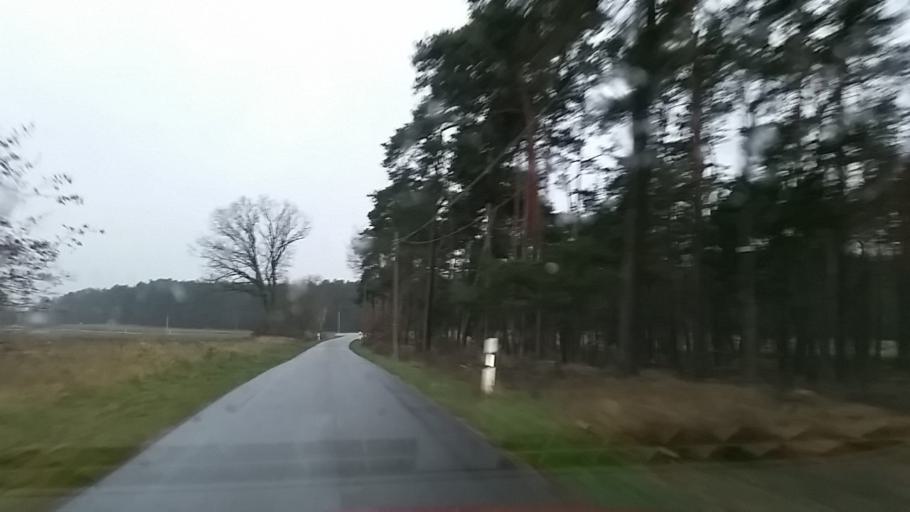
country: DE
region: Brandenburg
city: Gumtow
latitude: 53.0049
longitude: 12.2257
